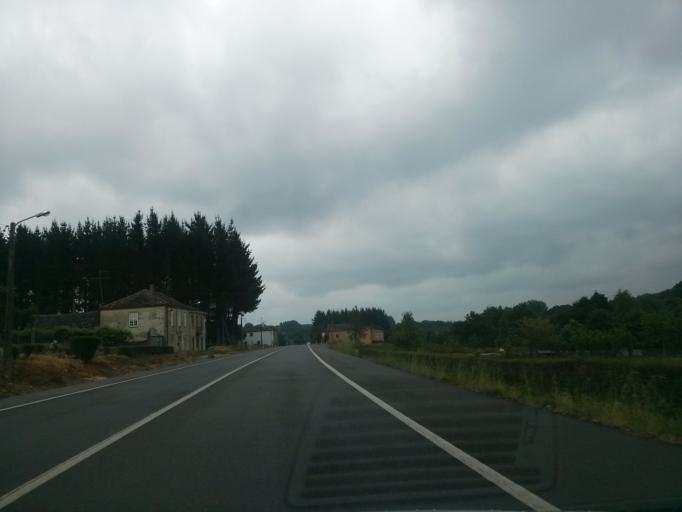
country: ES
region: Galicia
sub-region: Provincia de Lugo
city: Begonte
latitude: 43.1736
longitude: -7.7472
